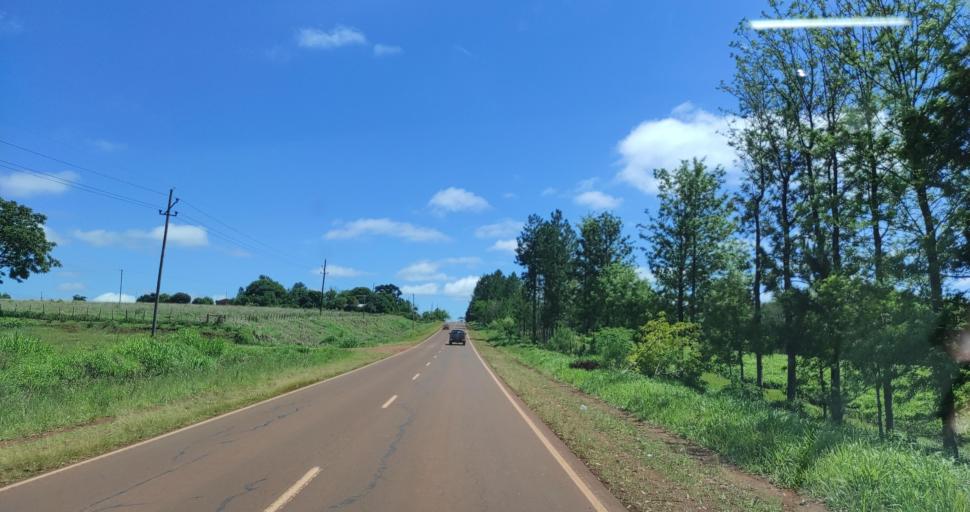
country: AR
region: Misiones
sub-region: Departamento de Veinticinco de Mayo
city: Veinticinco de Mayo
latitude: -27.4015
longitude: -54.7502
